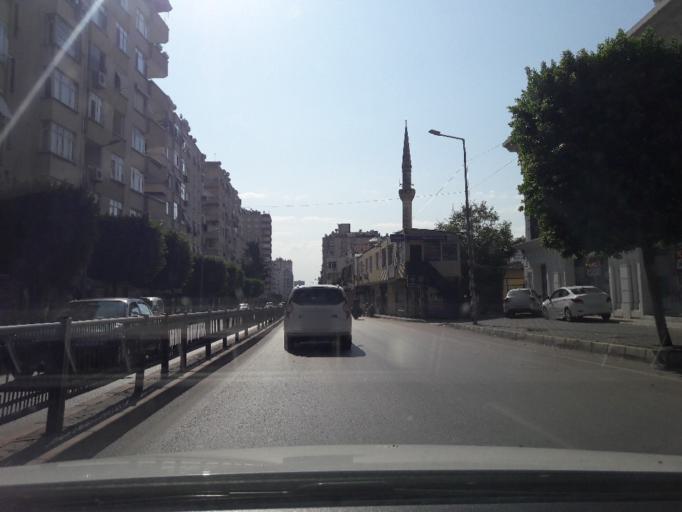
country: TR
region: Adana
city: Adana
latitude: 37.0128
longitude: 35.3227
